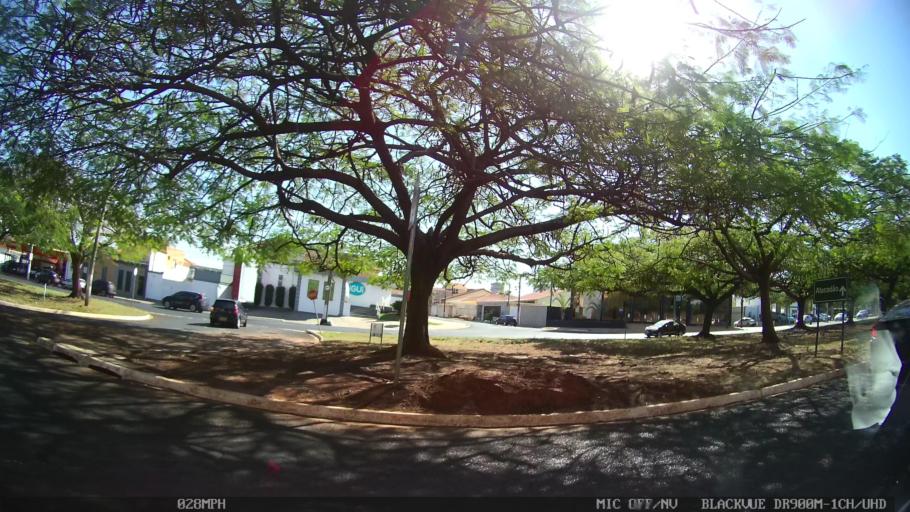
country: BR
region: Sao Paulo
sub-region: Ribeirao Preto
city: Ribeirao Preto
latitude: -21.2076
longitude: -47.7700
